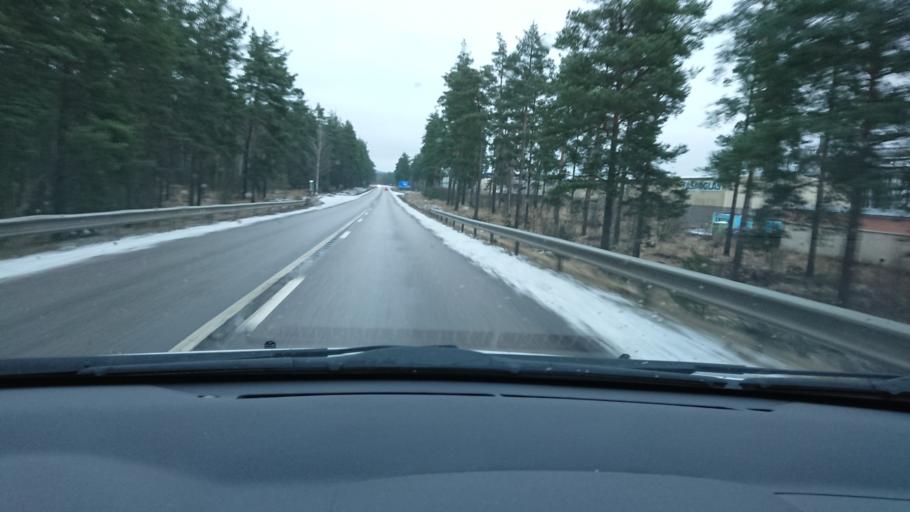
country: SE
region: Kalmar
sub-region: Hultsfreds Kommun
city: Hultsfred
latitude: 57.5061
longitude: 15.8293
